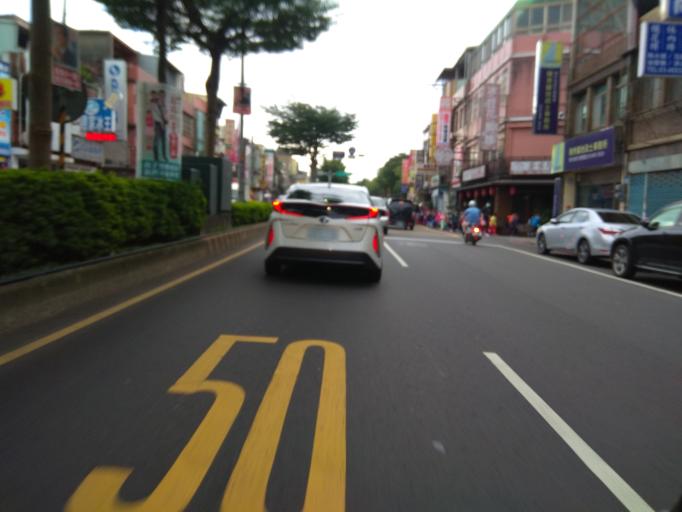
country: TW
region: Taiwan
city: Daxi
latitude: 24.8968
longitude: 121.2111
